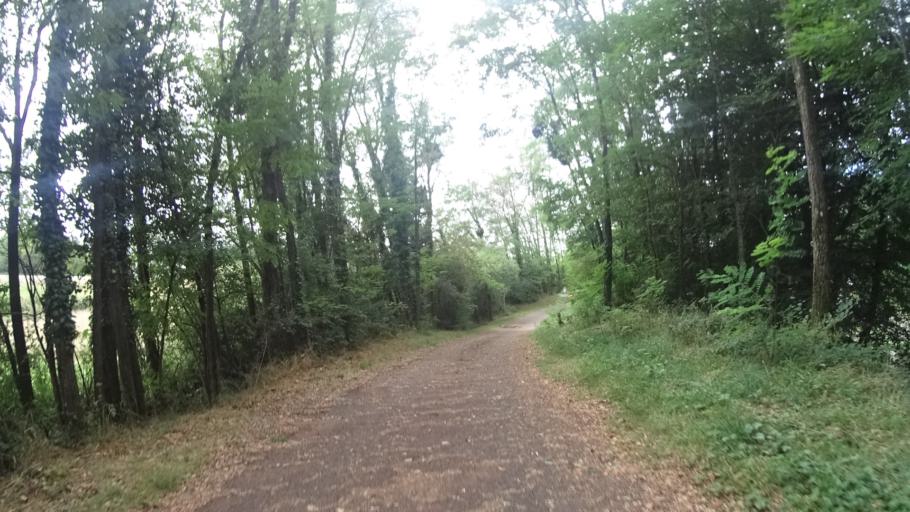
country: FR
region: Bourgogne
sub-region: Departement de Saone-et-Loire
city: Saint-Leu
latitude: 46.7505
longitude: 4.5009
